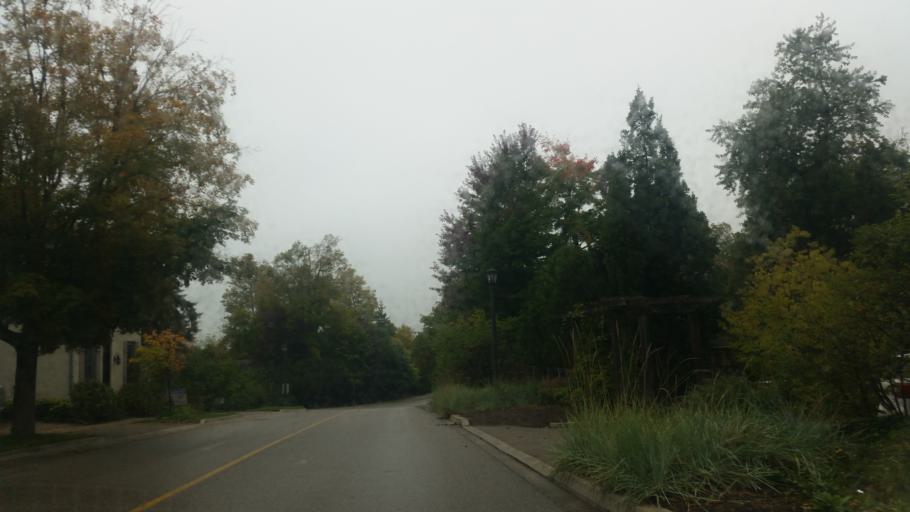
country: CA
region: Ontario
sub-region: Wellington County
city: Guelph
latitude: 43.6853
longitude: -80.4334
